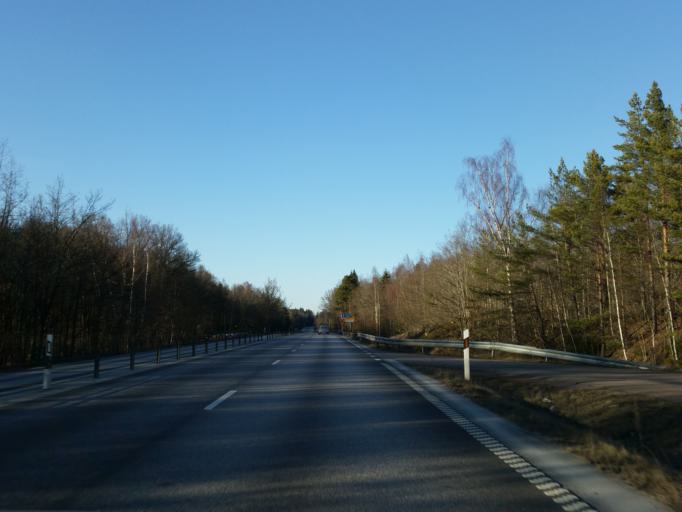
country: SE
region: Kalmar
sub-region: Oskarshamns Kommun
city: Oskarshamn
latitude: 57.3013
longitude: 16.4613
